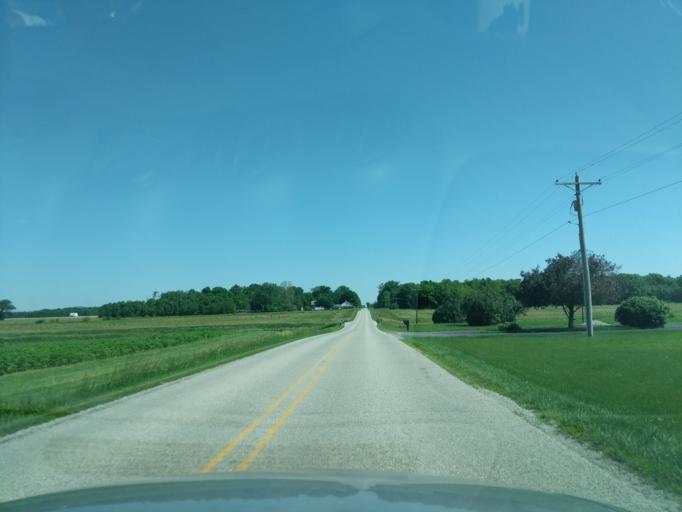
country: US
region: Indiana
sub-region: Huntington County
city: Huntington
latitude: 40.7740
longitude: -85.5074
